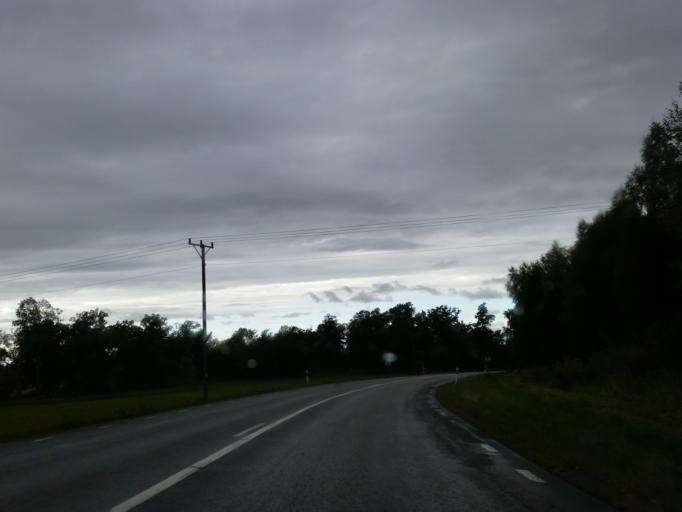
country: SE
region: Uppsala
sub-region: Enkopings Kommun
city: Dalby
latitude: 59.6510
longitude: 17.4145
